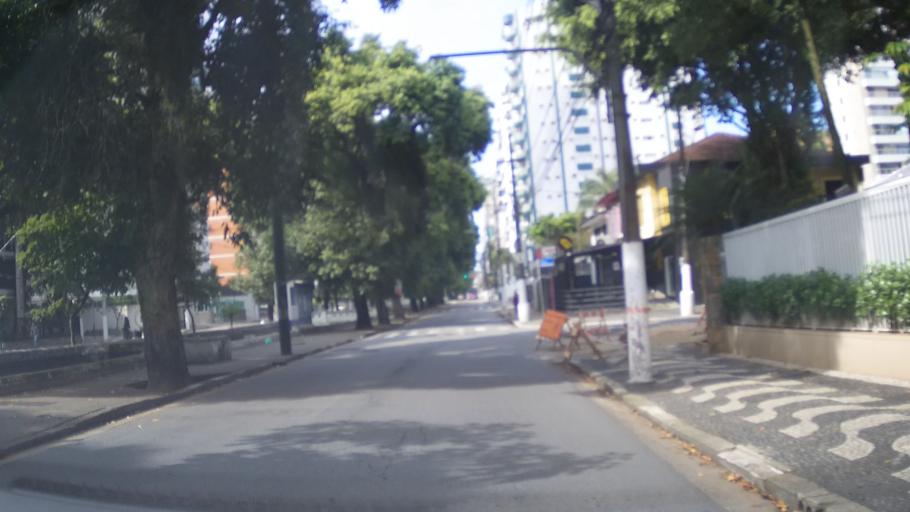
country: BR
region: Sao Paulo
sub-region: Santos
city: Santos
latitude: -23.9646
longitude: -46.3287
